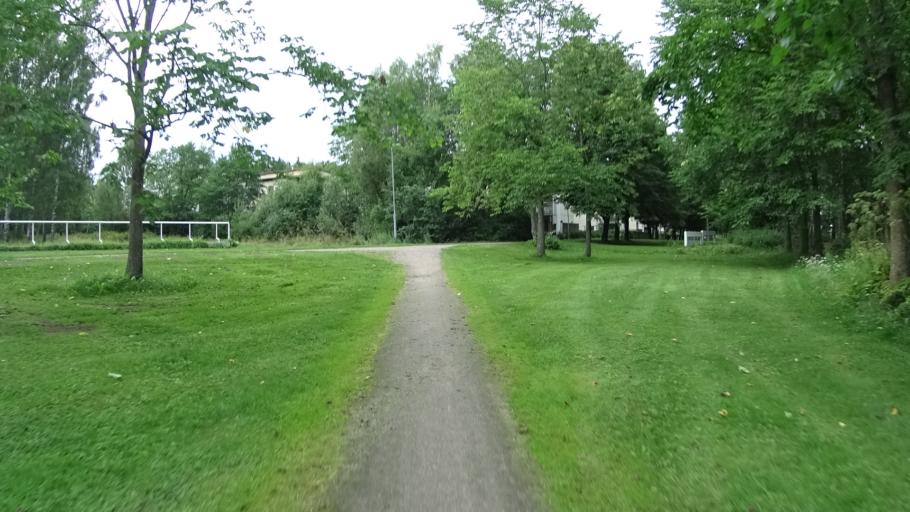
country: FI
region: Uusimaa
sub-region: Helsinki
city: Teekkarikylae
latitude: 60.2392
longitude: 24.8407
